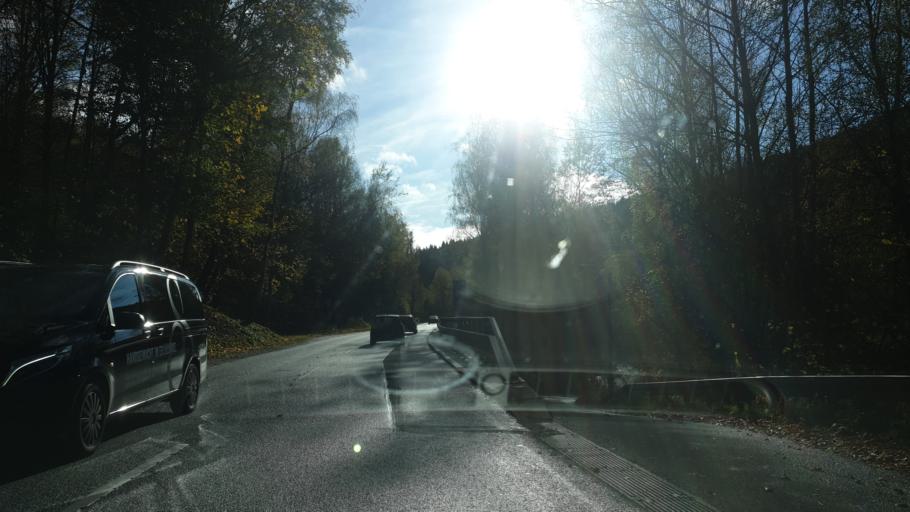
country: DE
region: Saxony
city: Aue
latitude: 50.5746
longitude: 12.6911
